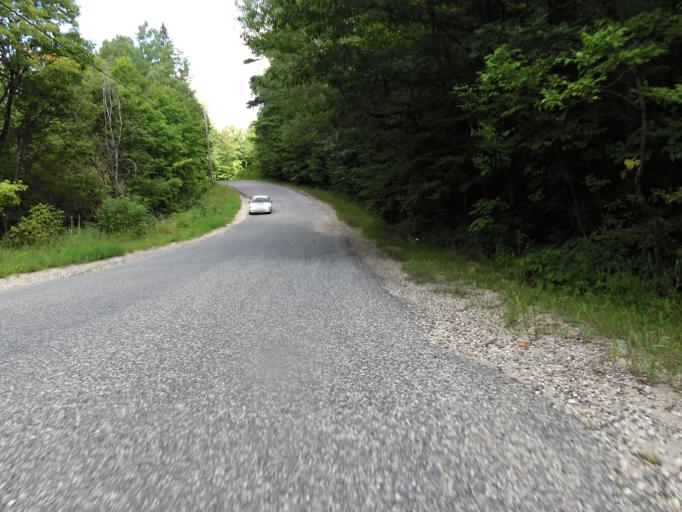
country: CA
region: Quebec
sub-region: Outaouais
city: Wakefield
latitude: 45.8100
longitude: -76.0301
